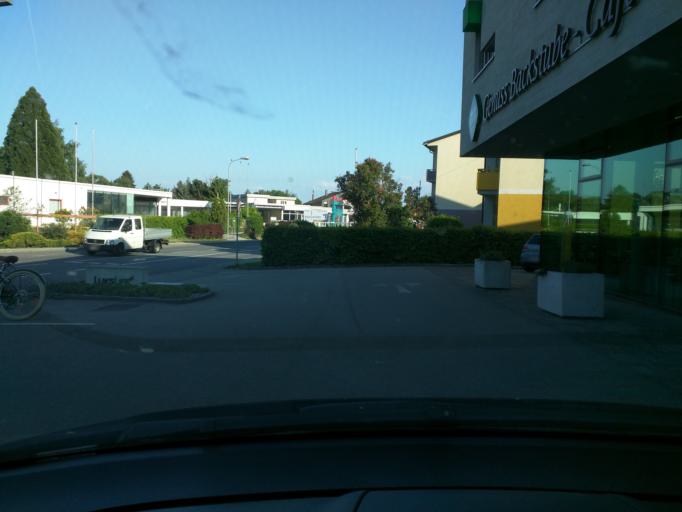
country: AT
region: Lower Austria
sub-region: Politischer Bezirk Melk
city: Ybbs an der Donau
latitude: 48.1757
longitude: 15.0832
